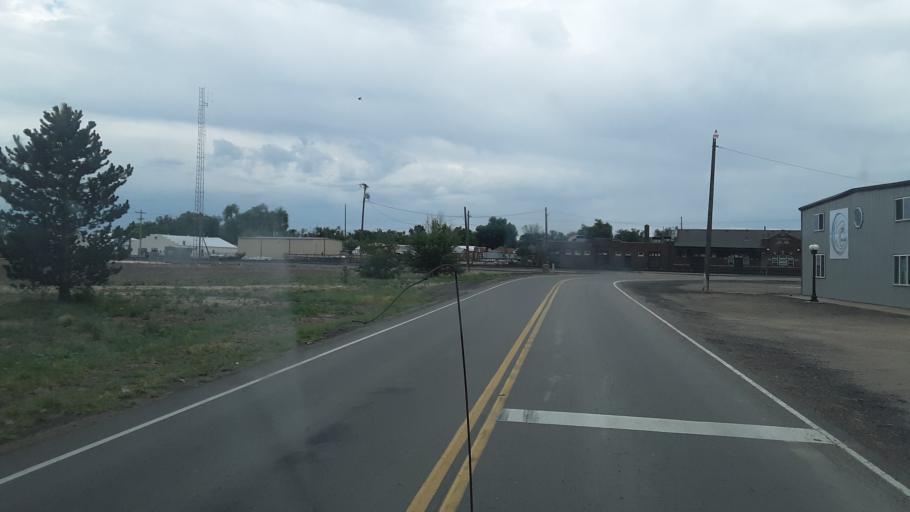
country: US
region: Colorado
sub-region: Otero County
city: Fowler
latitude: 38.1333
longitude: -104.0226
